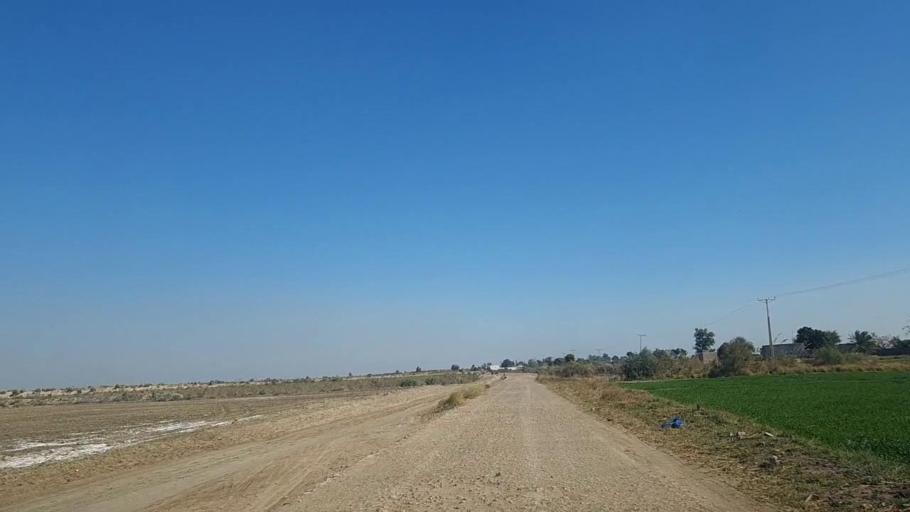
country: PK
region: Sindh
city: Sanghar
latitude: 26.2092
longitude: 68.8864
